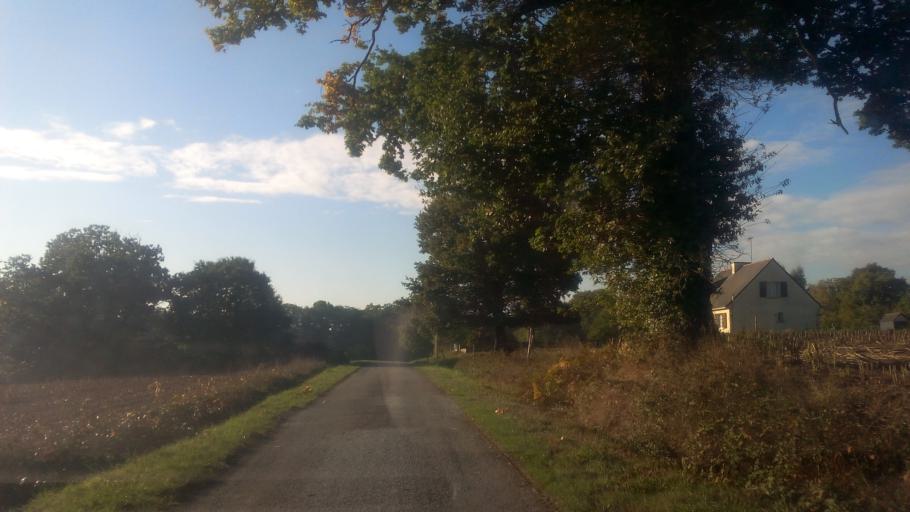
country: FR
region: Brittany
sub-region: Departement du Morbihan
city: Saint-Perreux
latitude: 47.6562
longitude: -2.1196
